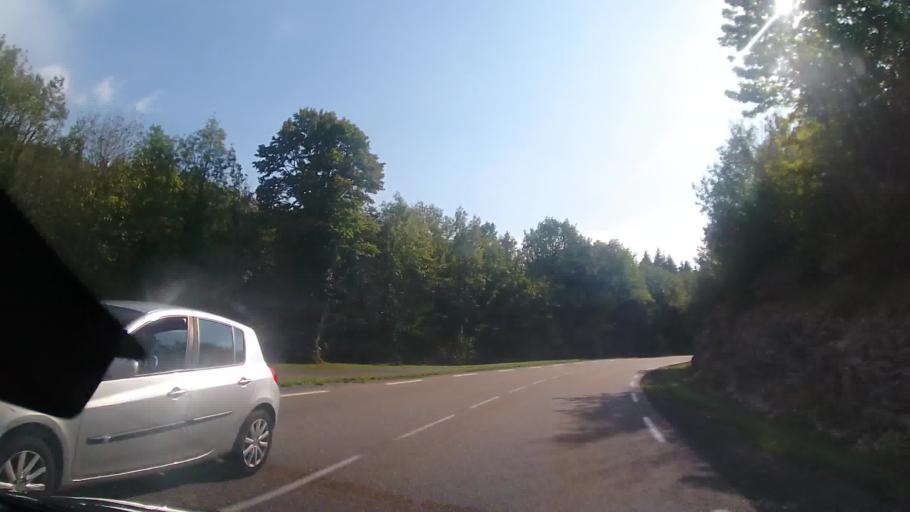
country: FR
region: Franche-Comte
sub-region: Departement du Jura
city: Clairvaux-les-Lacs
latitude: 46.5976
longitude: 5.8472
